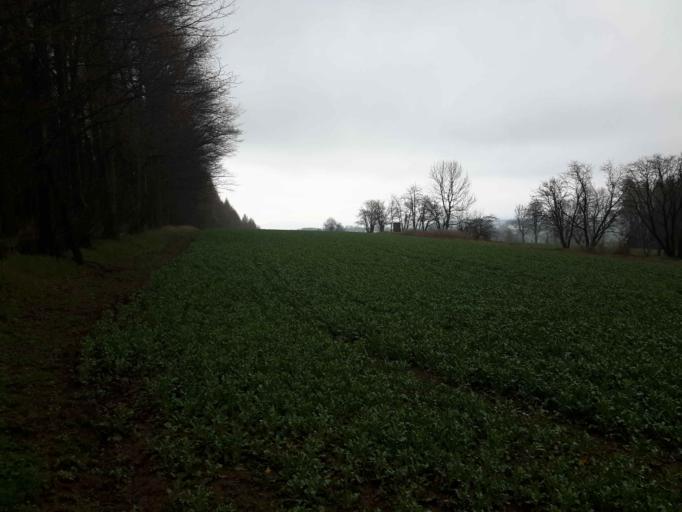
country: DE
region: Saxony
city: Sayda
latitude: 50.7255
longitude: 13.4174
